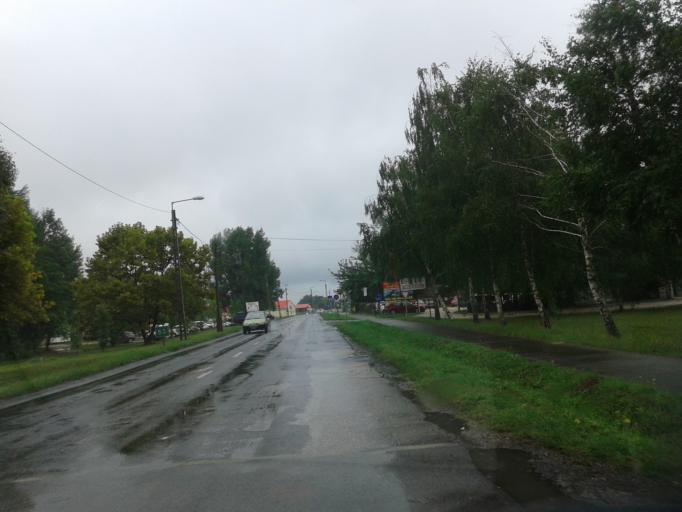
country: HU
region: Bacs-Kiskun
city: Kiskunhalas
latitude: 46.4554
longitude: 19.4670
